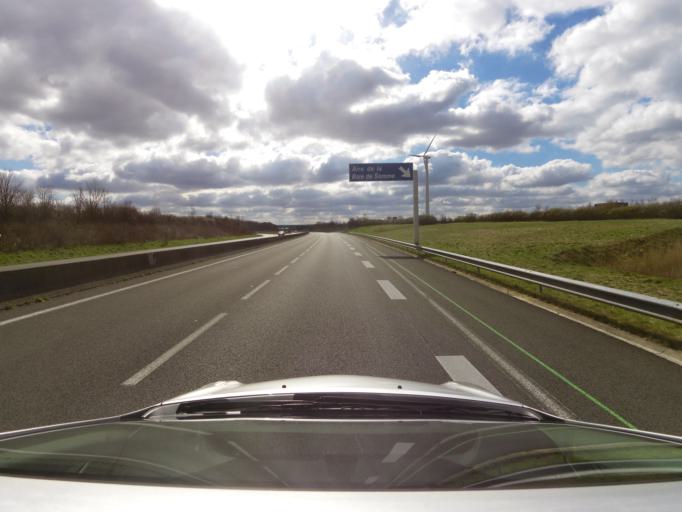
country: FR
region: Picardie
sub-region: Departement de la Somme
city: Sailly-Flibeaucourt
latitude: 50.1705
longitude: 1.7554
